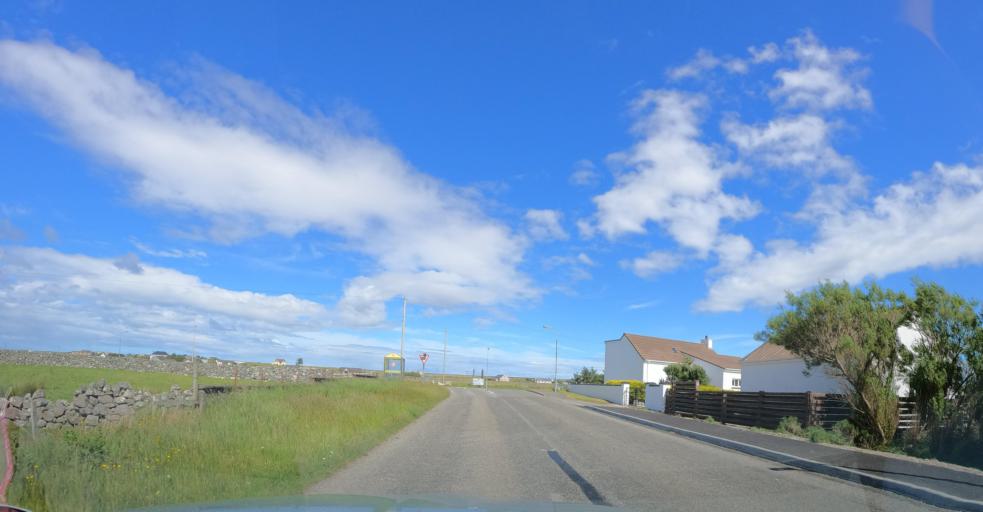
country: GB
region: Scotland
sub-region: Eilean Siar
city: Isle of Lewis
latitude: 58.3489
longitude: -6.5196
